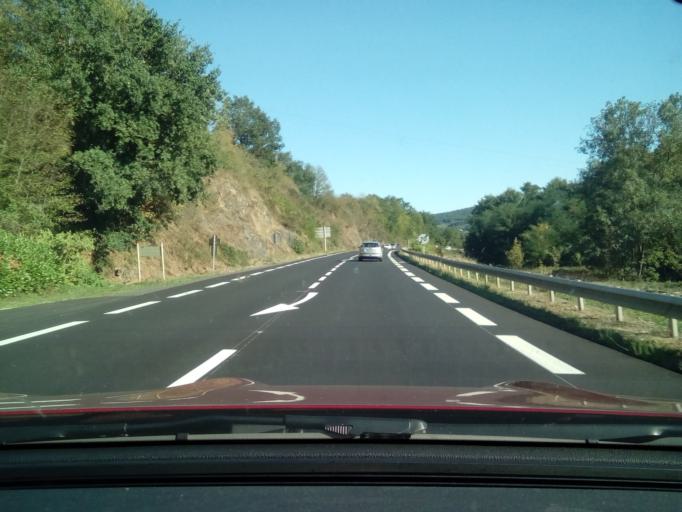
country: FR
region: Rhone-Alpes
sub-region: Departement du Rhone
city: Chatillon
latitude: 45.9008
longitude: 4.5859
